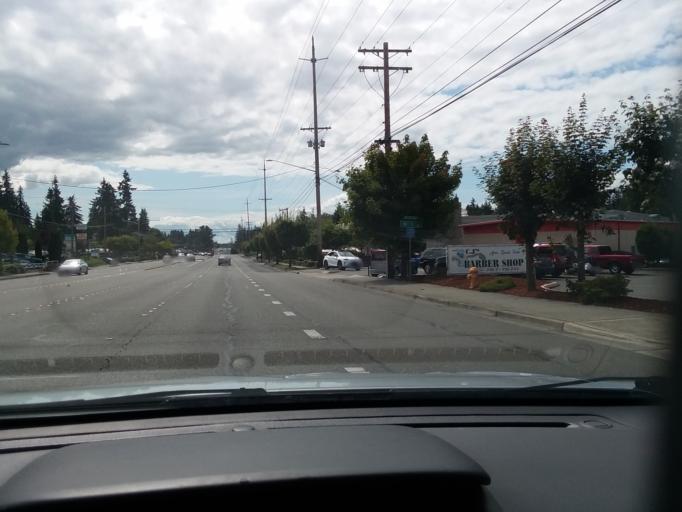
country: US
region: Washington
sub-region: Snohomish County
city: Lynnwood
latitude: 47.8367
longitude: -122.3018
